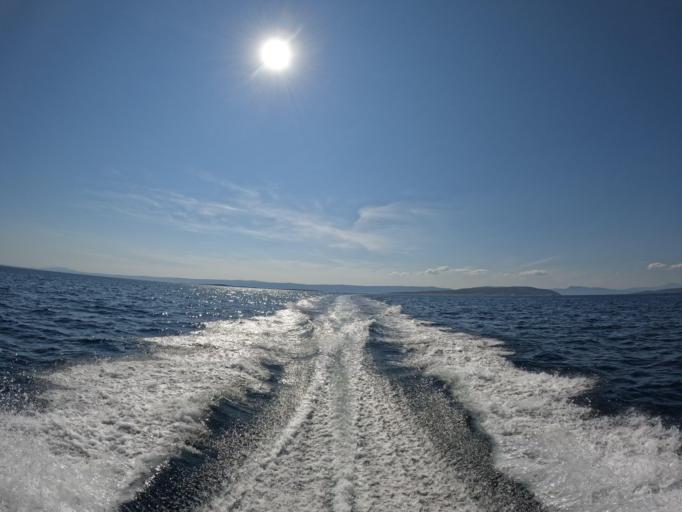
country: HR
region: Primorsko-Goranska
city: Punat
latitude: 44.9545
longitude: 14.5975
